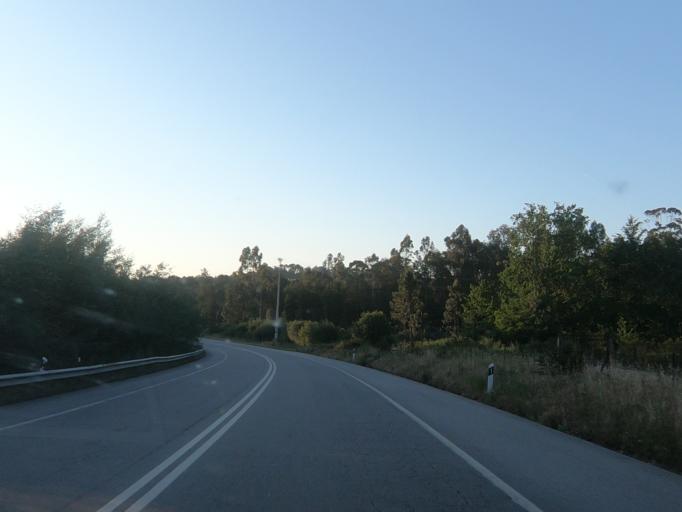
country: PT
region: Viseu
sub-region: Viseu
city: Rio de Loba
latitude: 40.6710
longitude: -7.8597
